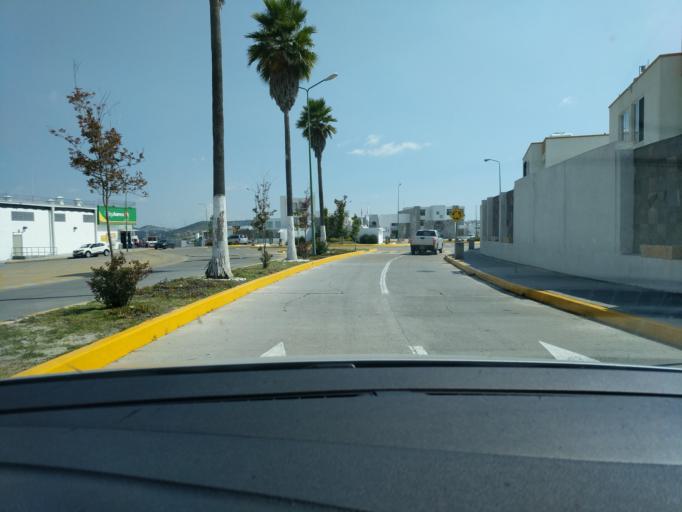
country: MX
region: Puebla
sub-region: Puebla
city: Galaxia la Calera
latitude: 19.0058
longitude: -98.1487
